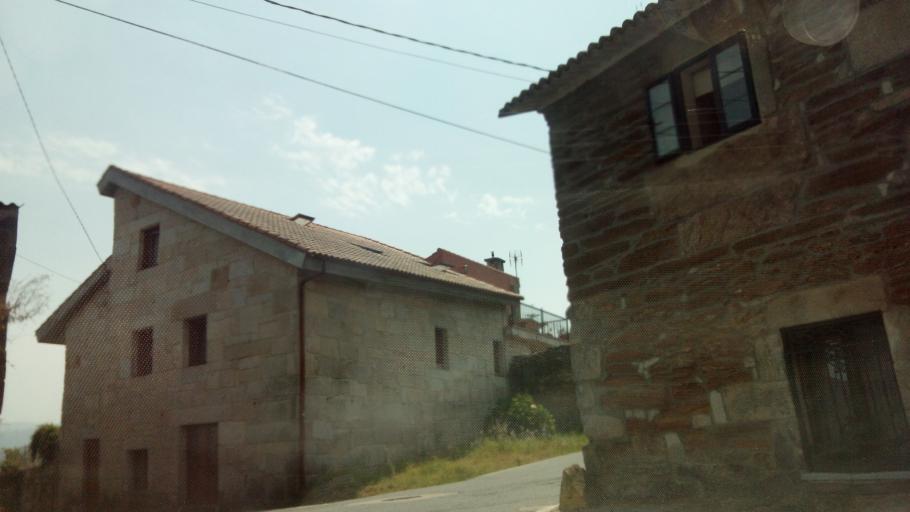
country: ES
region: Galicia
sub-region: Provincia de Pontevedra
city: Nigran
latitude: 42.1090
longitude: -8.8146
